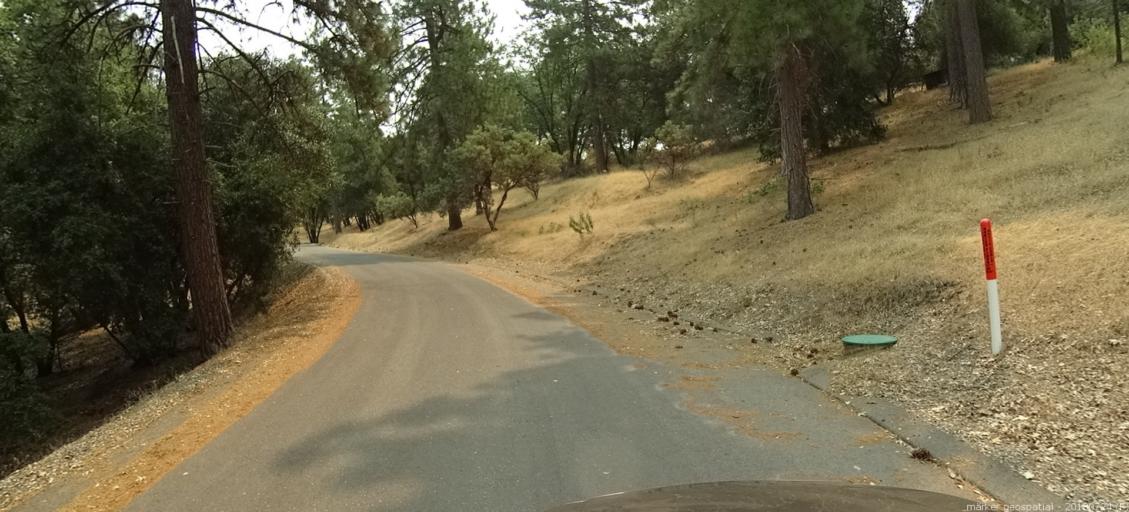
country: US
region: California
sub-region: Madera County
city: Oakhurst
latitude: 37.3247
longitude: -119.6050
